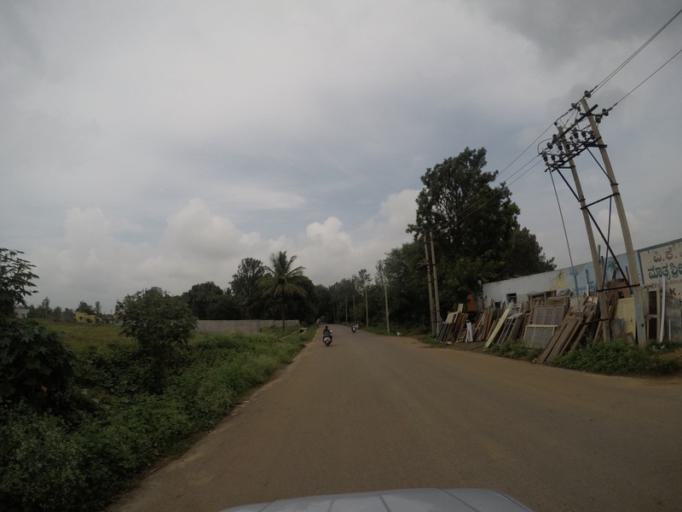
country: IN
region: Karnataka
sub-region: Bangalore Urban
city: Yelahanka
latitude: 13.1025
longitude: 77.5300
